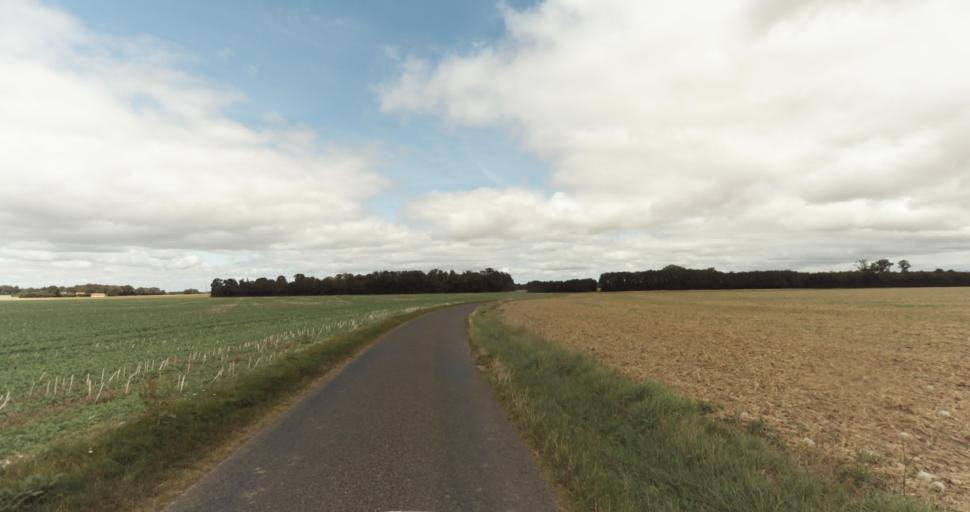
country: FR
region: Haute-Normandie
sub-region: Departement de l'Eure
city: La Madeleine-de-Nonancourt
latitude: 48.8958
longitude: 1.1992
